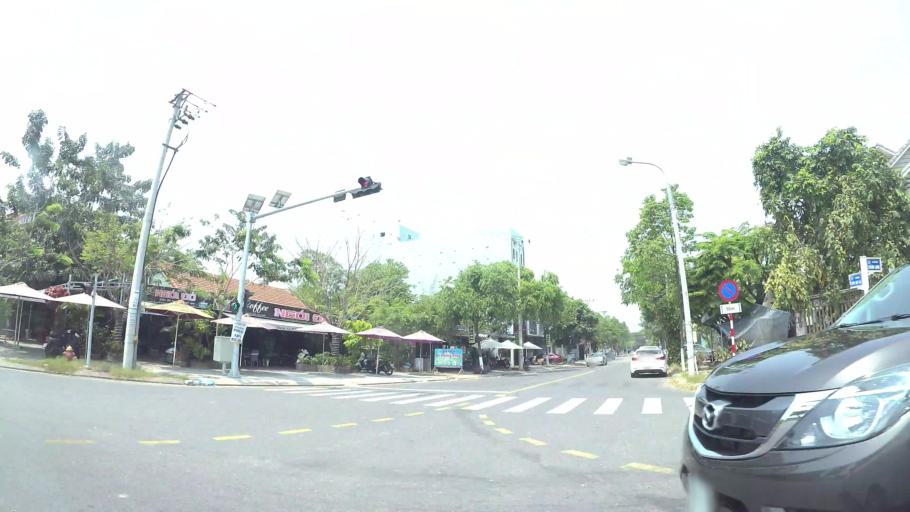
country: VN
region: Da Nang
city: Cam Le
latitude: 16.0152
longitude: 108.2098
